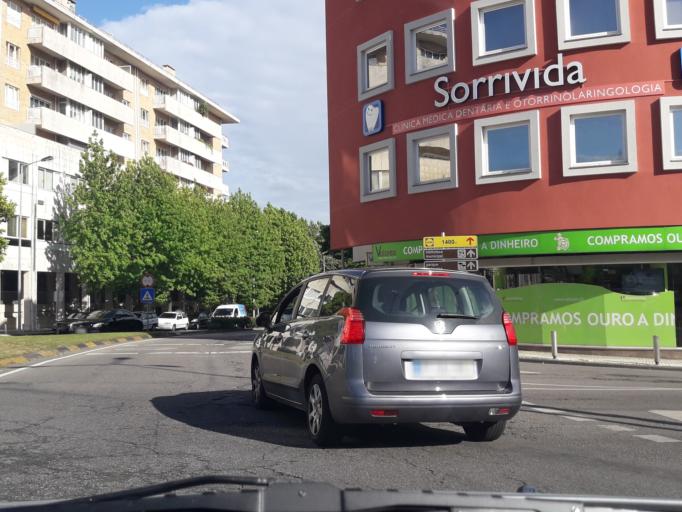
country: PT
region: Braga
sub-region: Vila Nova de Famalicao
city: Vila Nova de Famalicao
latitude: 41.4143
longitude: -8.5194
